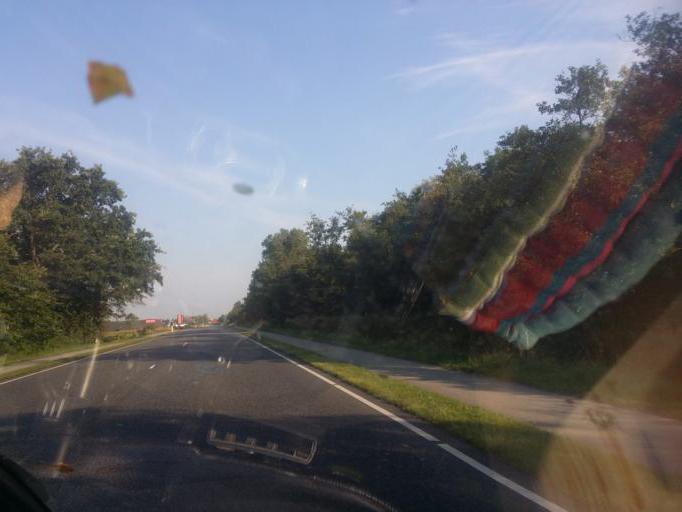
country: DK
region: South Denmark
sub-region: Tonder Kommune
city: Sherrebek
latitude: 55.1648
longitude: 8.7607
